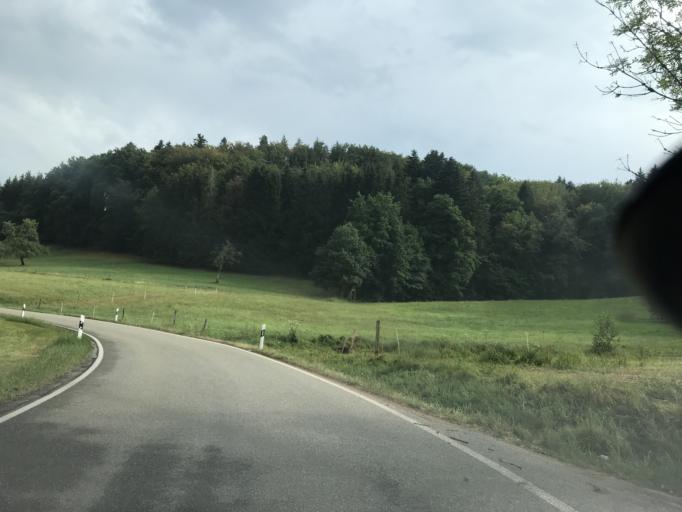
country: DE
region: Baden-Wuerttemberg
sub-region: Freiburg Region
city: Steinen
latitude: 47.6940
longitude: 7.7291
